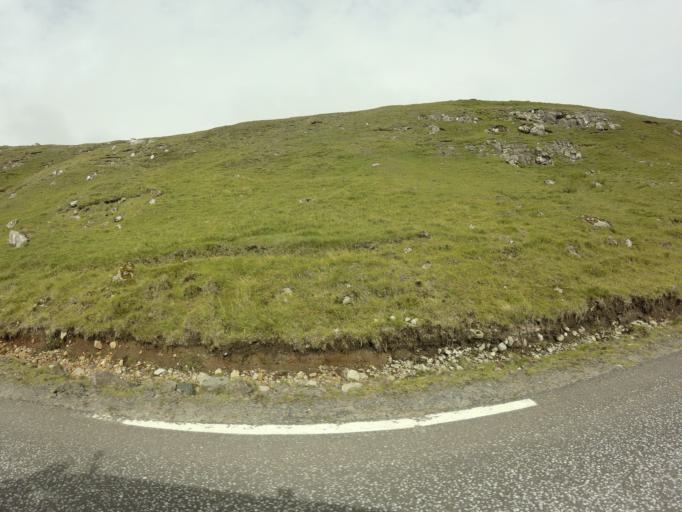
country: FO
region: Sandoy
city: Sandur
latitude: 61.8265
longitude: -6.7472
